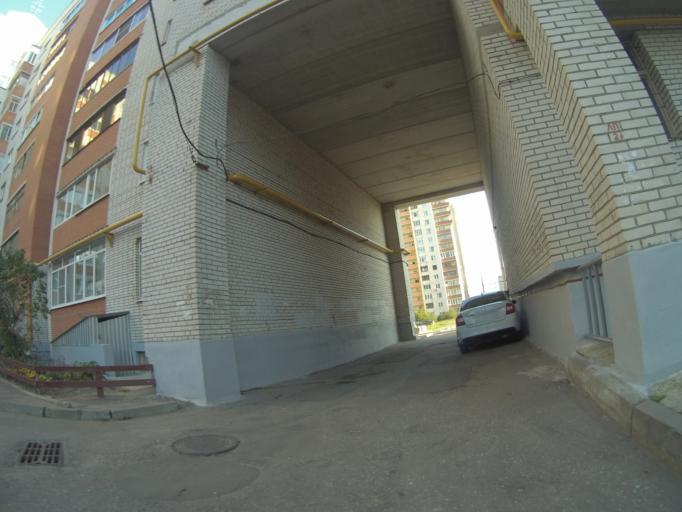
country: RU
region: Vladimir
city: Vladimir
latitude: 56.1057
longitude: 40.3482
